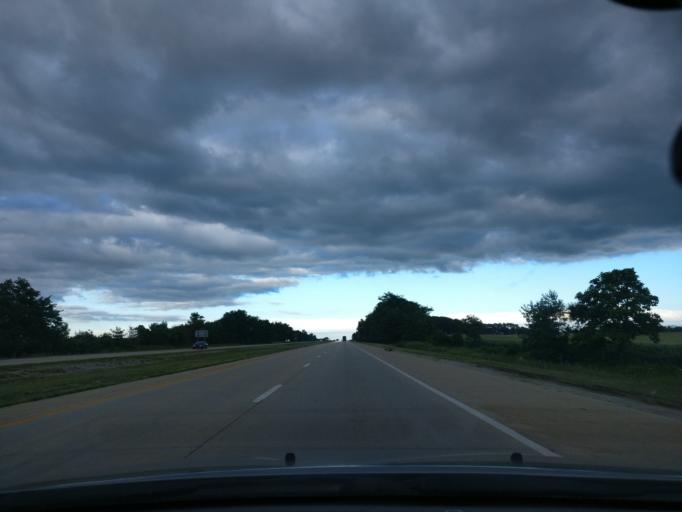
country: US
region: Ohio
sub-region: Greene County
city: Wilberforce
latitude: 39.6907
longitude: -83.8751
